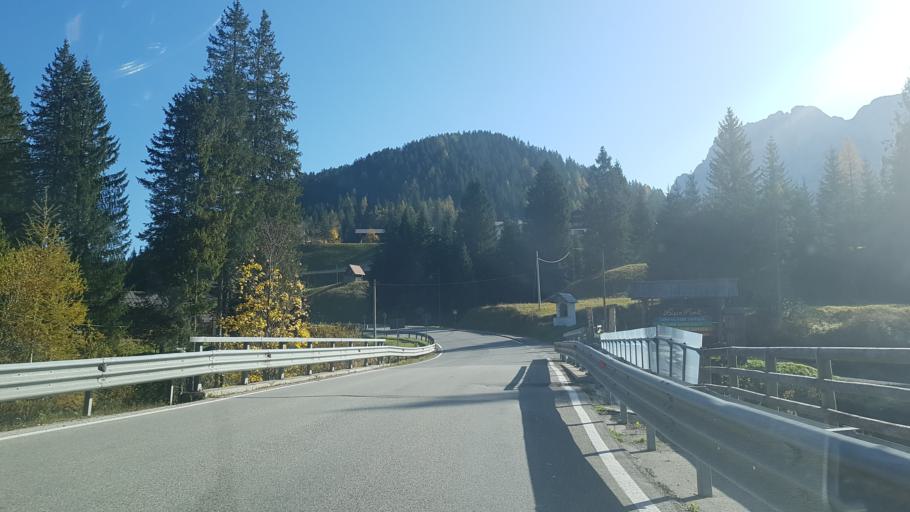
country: IT
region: Veneto
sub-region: Provincia di Belluno
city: Granvilla
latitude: 46.5716
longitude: 12.7184
